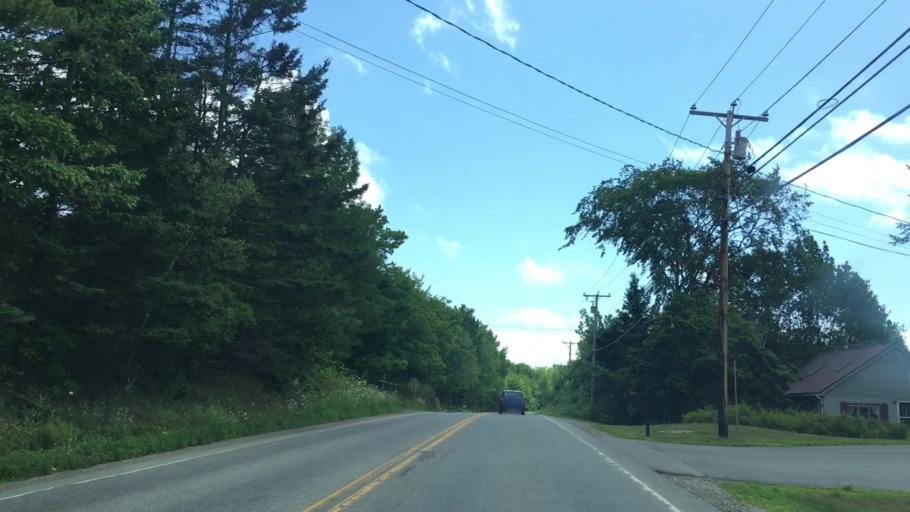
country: US
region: Maine
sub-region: Penobscot County
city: Hermon
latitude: 44.8036
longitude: -68.8976
